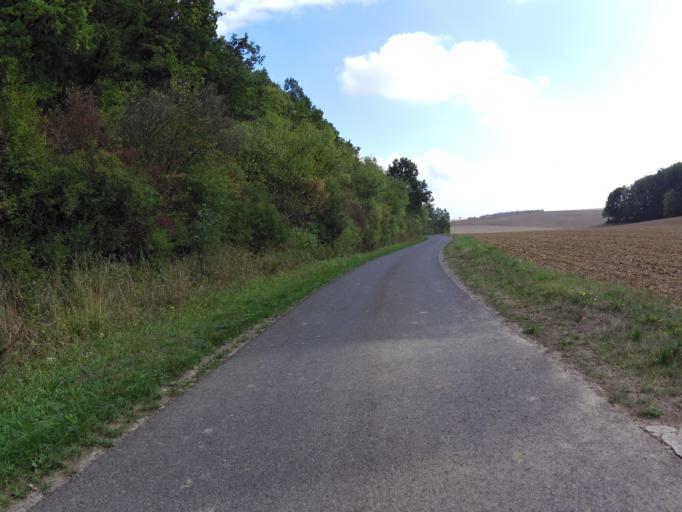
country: DE
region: Bavaria
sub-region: Regierungsbezirk Unterfranken
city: Waldbrunn
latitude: 49.7756
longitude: 9.8100
